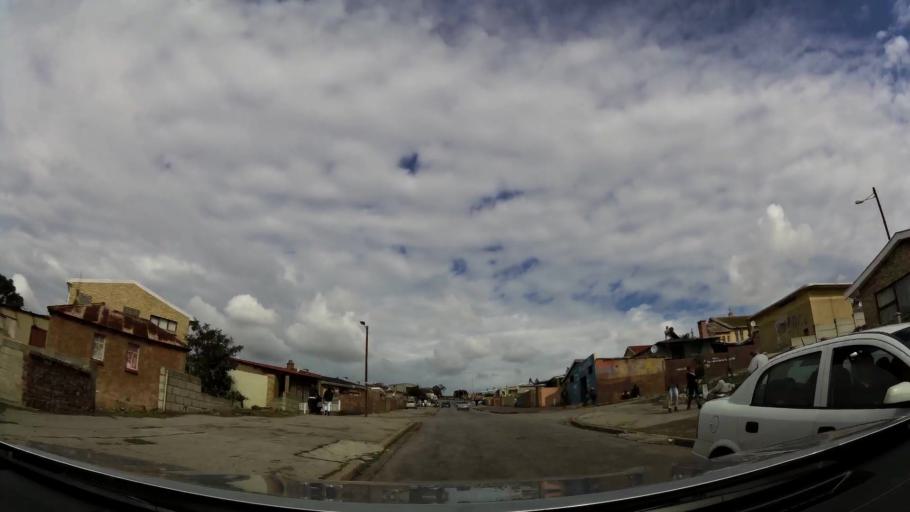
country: ZA
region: Eastern Cape
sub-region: Nelson Mandela Bay Metropolitan Municipality
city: Port Elizabeth
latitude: -33.9327
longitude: 25.5729
